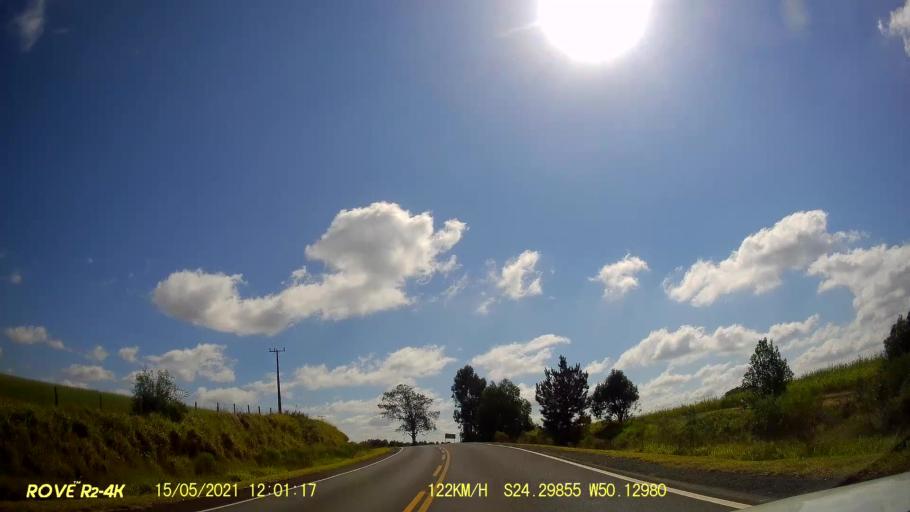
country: BR
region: Parana
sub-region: Pirai Do Sul
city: Pirai do Sul
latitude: -24.2987
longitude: -50.1300
